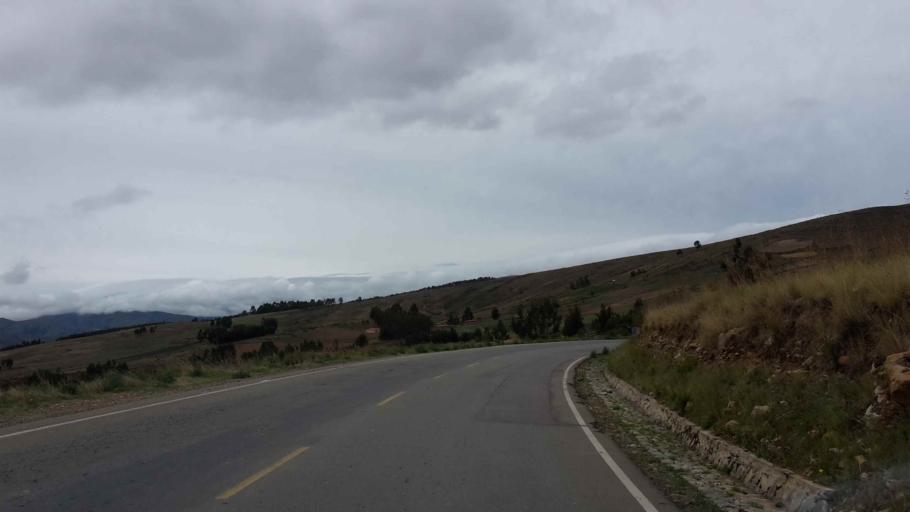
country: BO
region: Cochabamba
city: Arani
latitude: -17.4645
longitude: -65.6727
